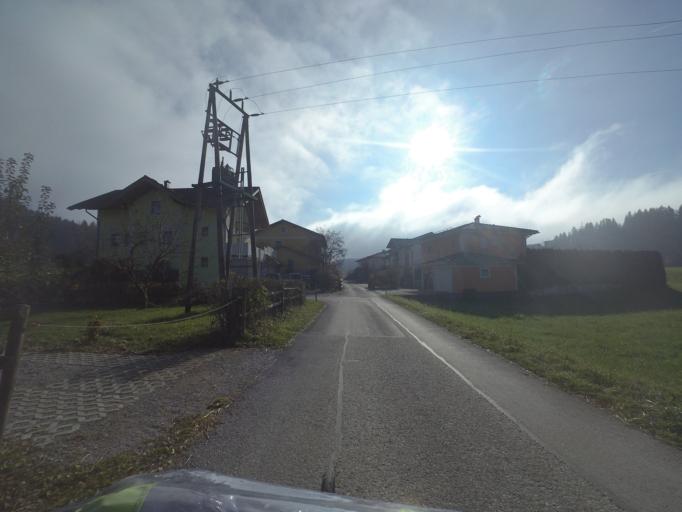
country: AT
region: Salzburg
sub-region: Politischer Bezirk Hallein
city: Adnet
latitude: 47.6825
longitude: 13.1438
